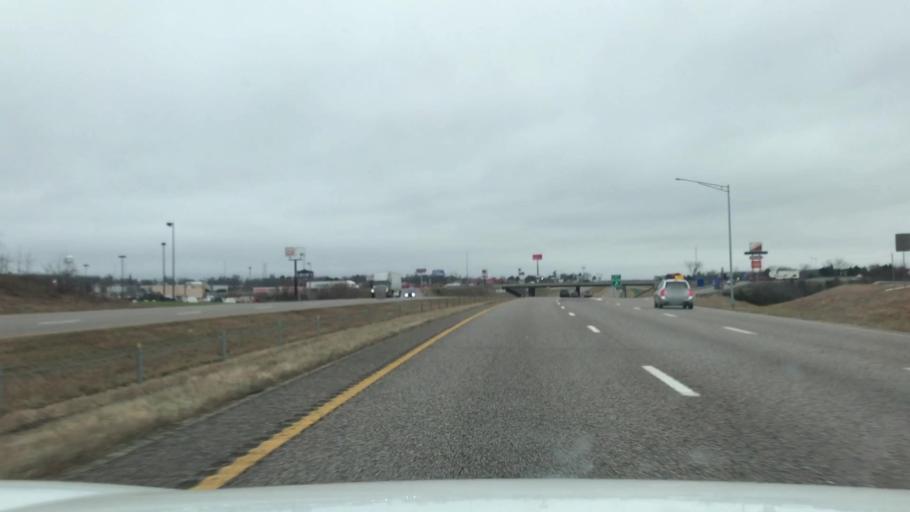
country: US
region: Missouri
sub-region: Franklin County
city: Sullivan
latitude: 38.2270
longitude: -91.1530
